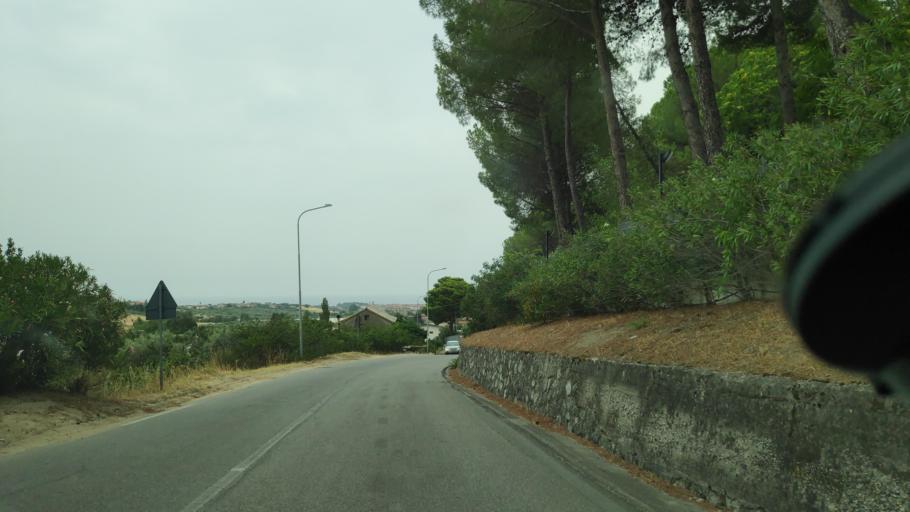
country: IT
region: Calabria
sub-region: Provincia di Catanzaro
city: Martelli-Laganosa
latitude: 38.6673
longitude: 16.5209
